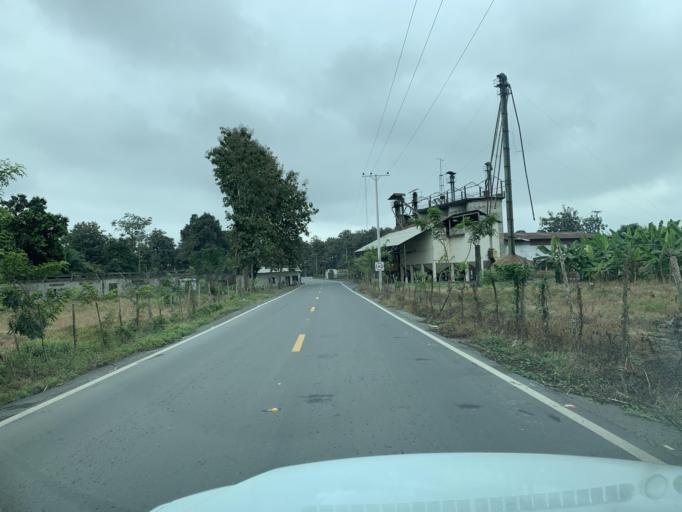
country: EC
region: Guayas
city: Coronel Marcelino Mariduena
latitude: -2.2956
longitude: -79.5036
